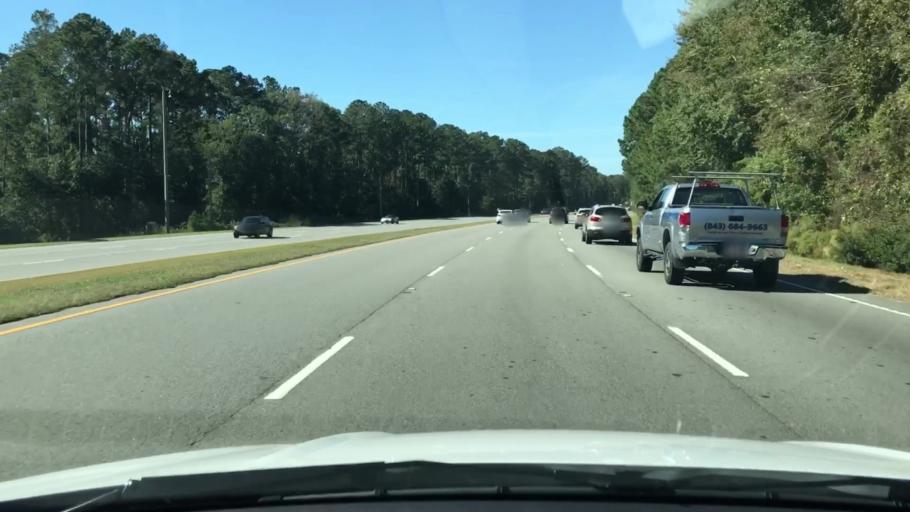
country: US
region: South Carolina
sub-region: Beaufort County
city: Bluffton
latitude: 32.2868
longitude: -80.8910
